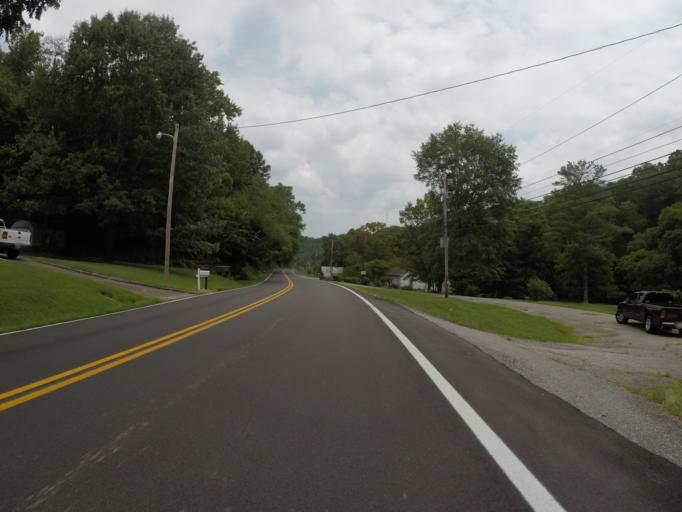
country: US
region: Kentucky
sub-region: Boyd County
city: Catlettsburg
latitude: 38.4183
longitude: -82.6180
